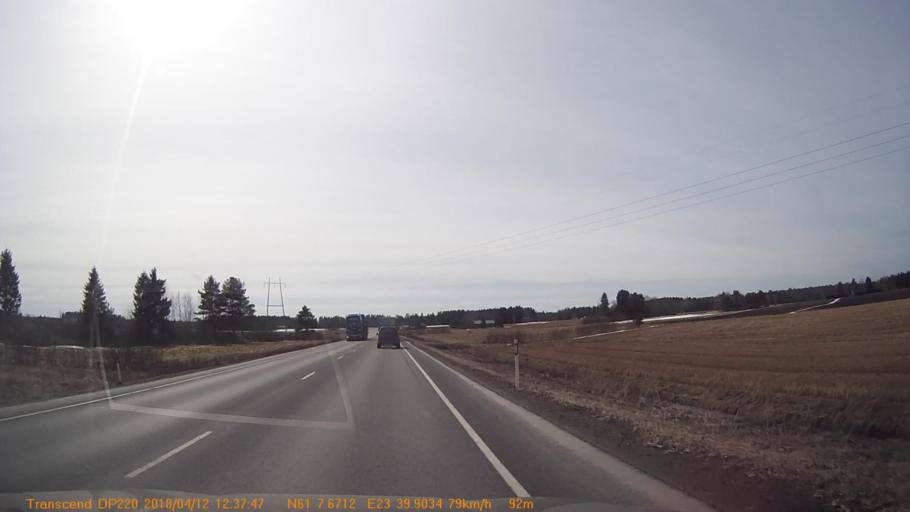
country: FI
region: Pirkanmaa
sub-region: Etelae-Pirkanmaa
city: Kylmaekoski
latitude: 61.1281
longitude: 23.6653
